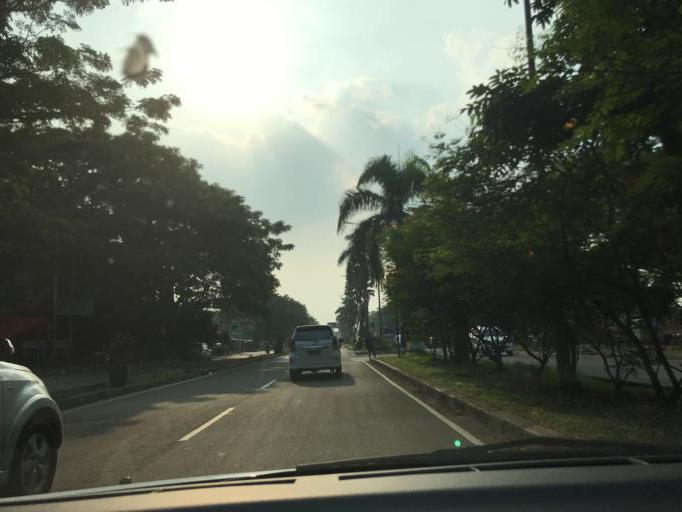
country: ID
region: West Java
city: Cibinong
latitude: -6.5205
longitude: 106.8387
